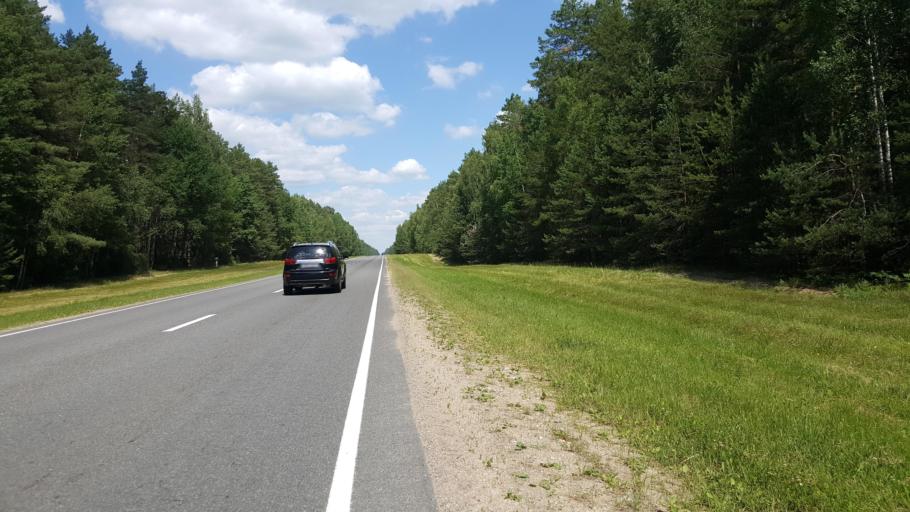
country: BY
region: Brest
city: Kamyanyuki
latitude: 52.5102
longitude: 23.7886
